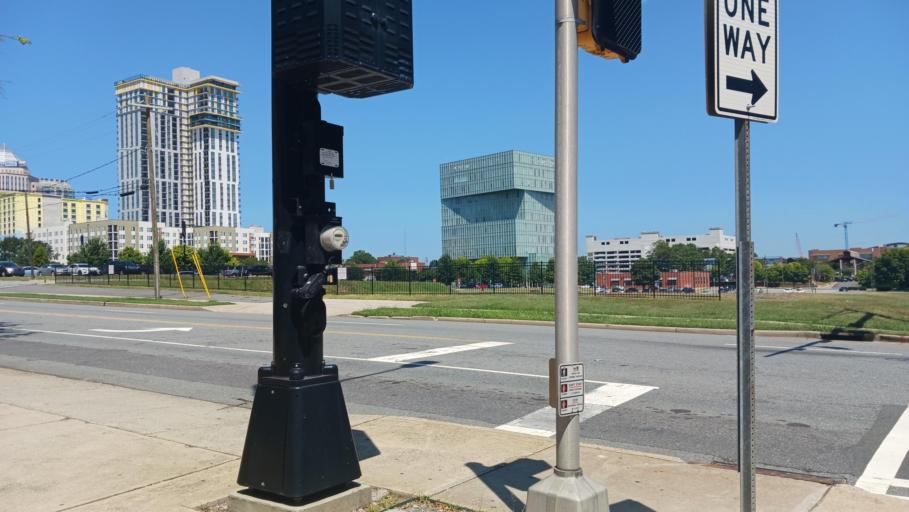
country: US
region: North Carolina
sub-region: Mecklenburg County
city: Charlotte
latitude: 35.2260
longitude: -80.8359
